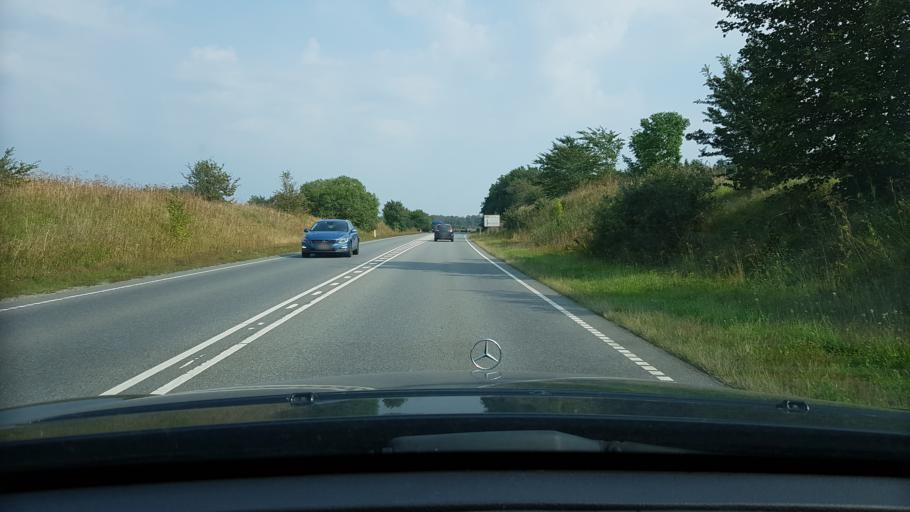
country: DK
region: North Denmark
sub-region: Alborg Kommune
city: Klarup
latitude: 57.0214
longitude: 10.0412
